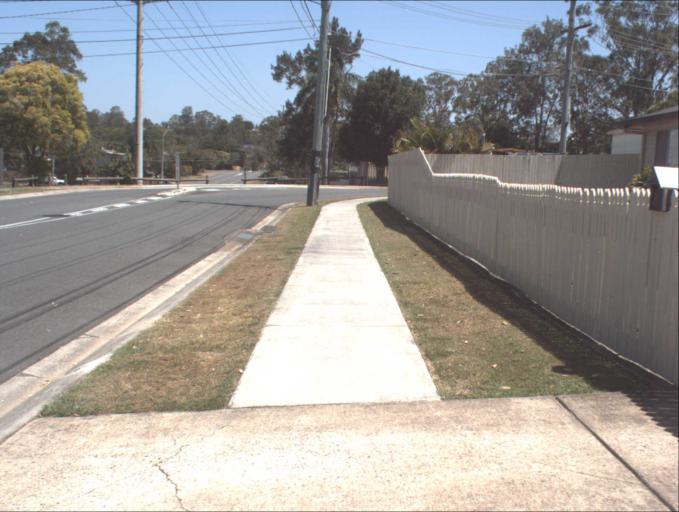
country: AU
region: Queensland
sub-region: Logan
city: Beenleigh
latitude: -27.6897
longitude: 153.1795
